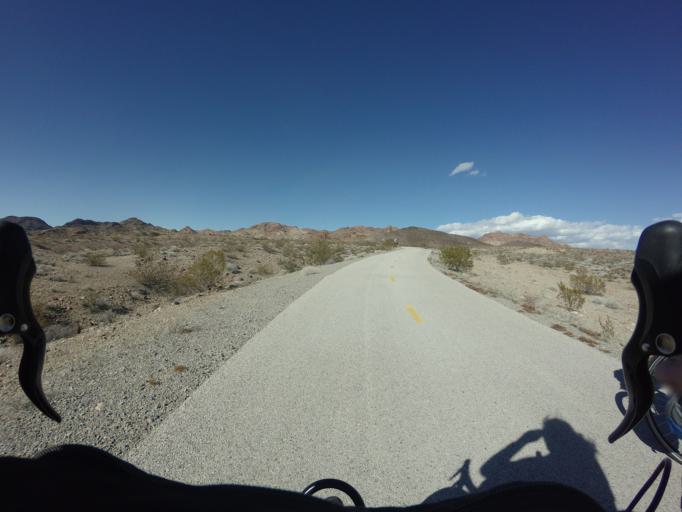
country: US
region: Nevada
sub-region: Clark County
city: Boulder City
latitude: 35.9699
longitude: -114.8760
